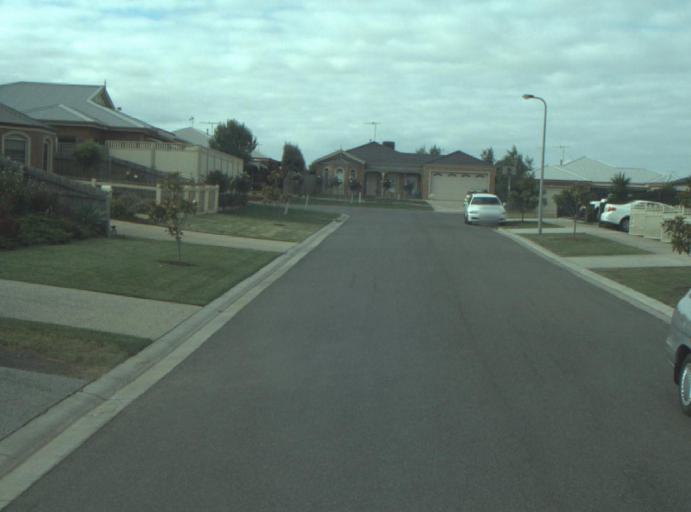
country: AU
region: Victoria
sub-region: Greater Geelong
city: Wandana Heights
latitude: -38.2096
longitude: 144.3128
